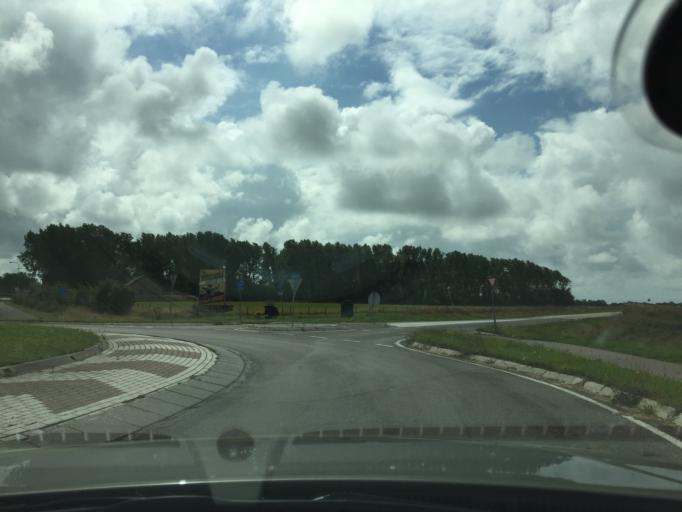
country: NL
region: North Holland
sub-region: Gemeente Texel
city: Den Burg
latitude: 53.0581
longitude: 4.7838
